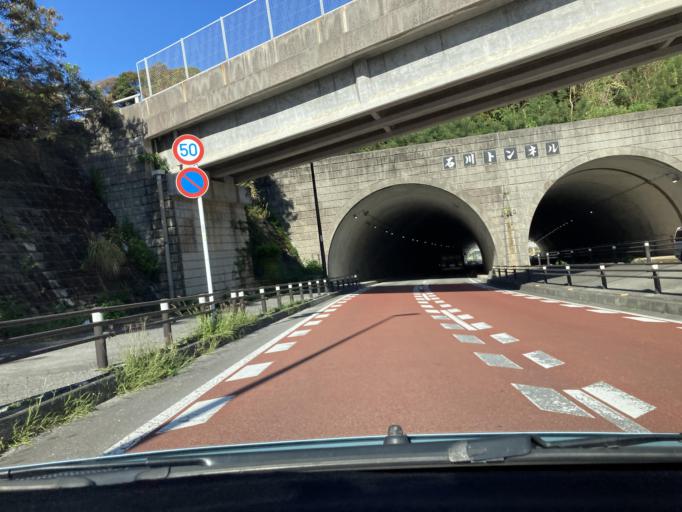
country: JP
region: Okinawa
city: Ishikawa
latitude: 26.4223
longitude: 127.8151
